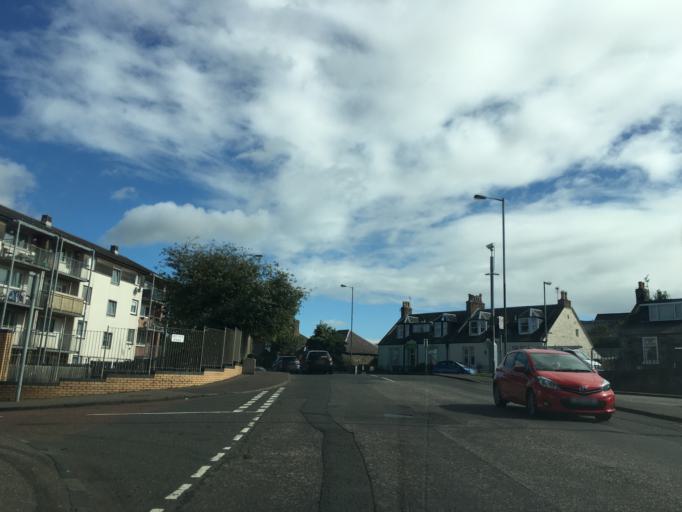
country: GB
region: Scotland
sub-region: Midlothian
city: Loanhead
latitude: 55.9037
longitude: -3.1381
